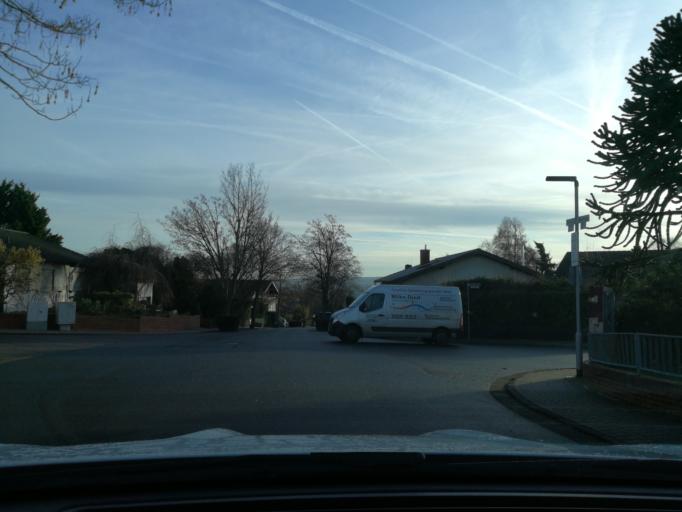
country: DE
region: Hesse
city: Reinheim
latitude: 49.8321
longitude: 8.8251
